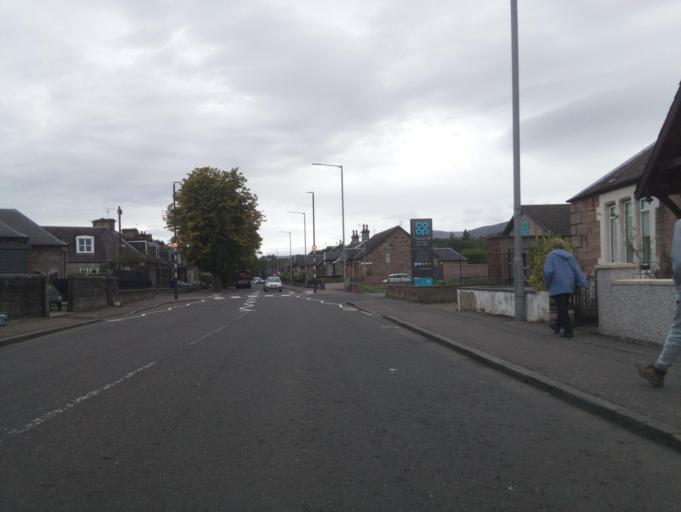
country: GB
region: Scotland
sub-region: Clackmannanshire
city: Alloa
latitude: 56.1207
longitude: -3.7992
